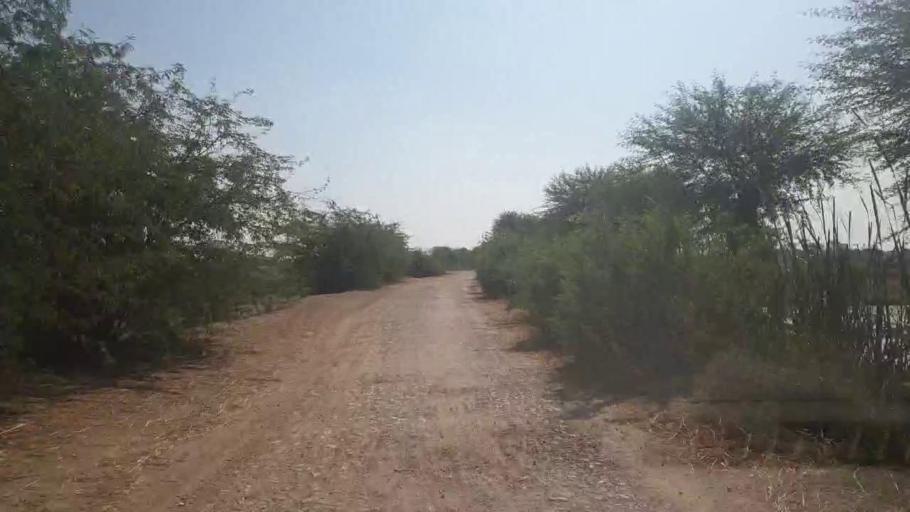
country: PK
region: Sindh
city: Badin
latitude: 24.6048
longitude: 68.8546
